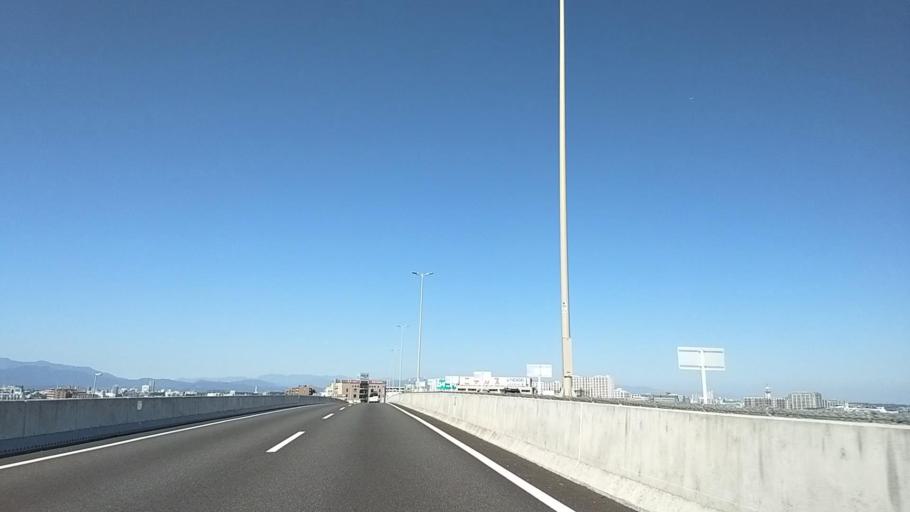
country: JP
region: Kanagawa
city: Minami-rinkan
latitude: 35.5050
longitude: 139.4824
